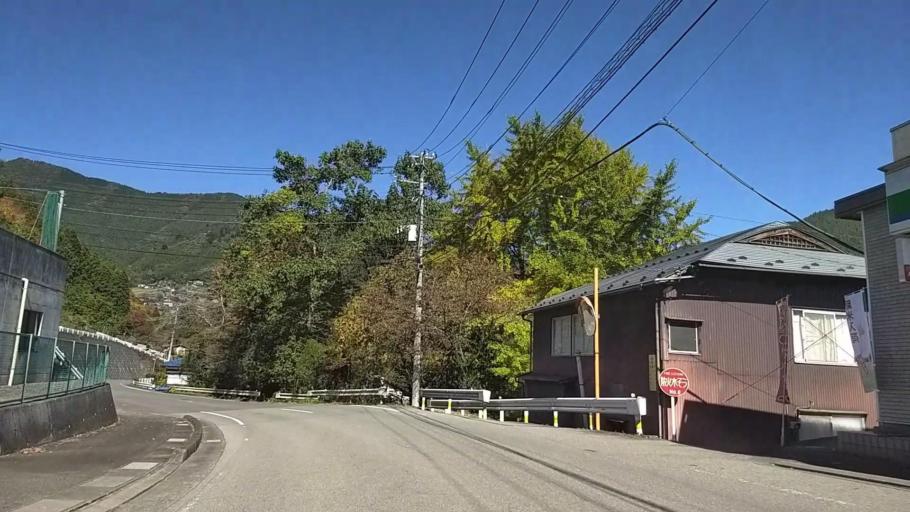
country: JP
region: Yamanashi
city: Uenohara
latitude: 35.6670
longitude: 139.0883
